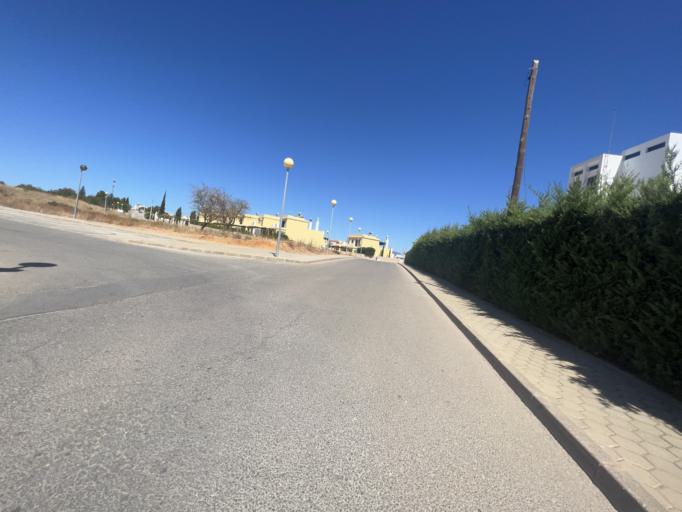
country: PT
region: Faro
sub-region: Portimao
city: Portimao
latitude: 37.1291
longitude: -8.5115
